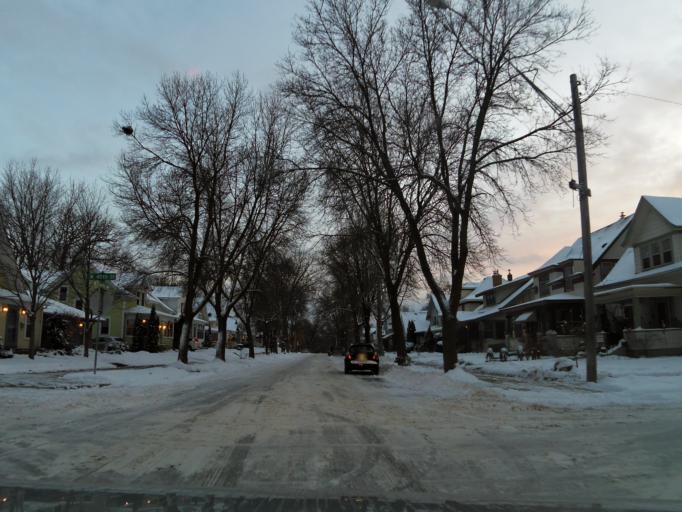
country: US
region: Minnesota
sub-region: Hennepin County
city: Saint Louis Park
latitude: 44.9216
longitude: -93.3215
